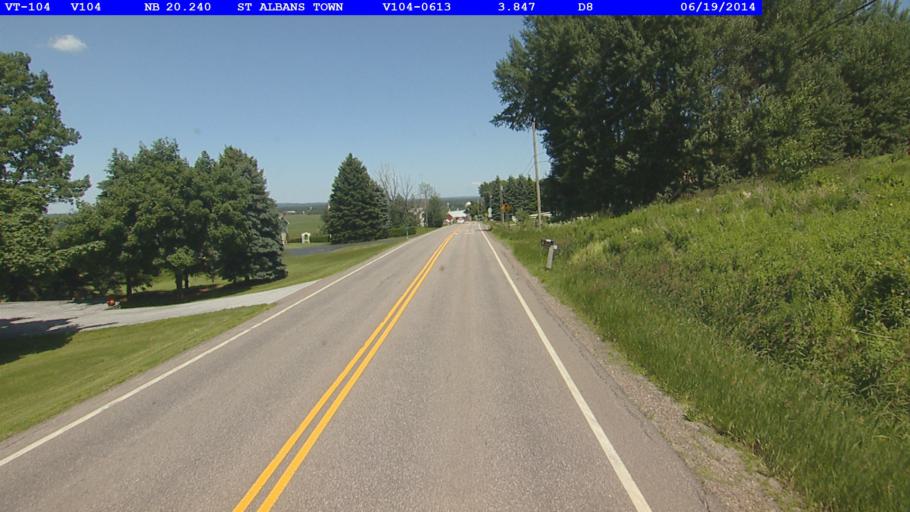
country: US
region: Vermont
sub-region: Franklin County
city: Saint Albans
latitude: 44.8255
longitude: -73.0555
